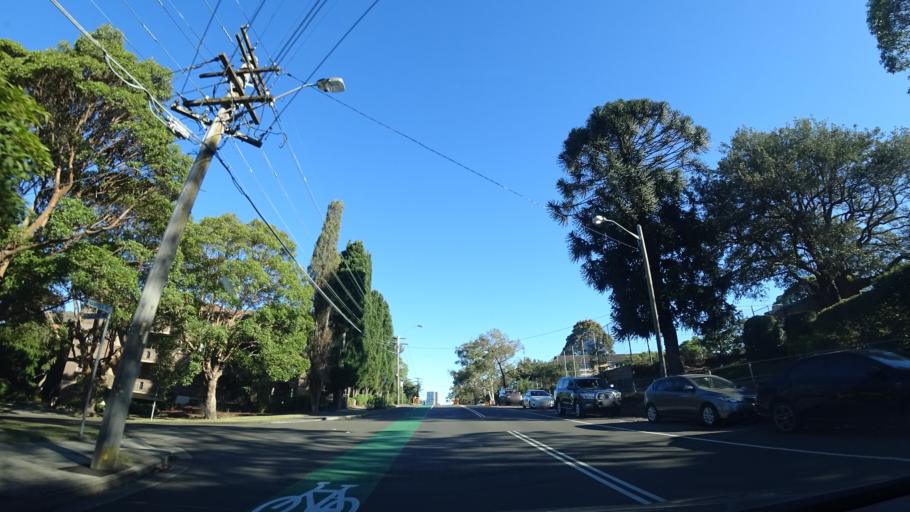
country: AU
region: New South Wales
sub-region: Willoughby
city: Artarmon
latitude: -33.8112
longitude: 151.1876
